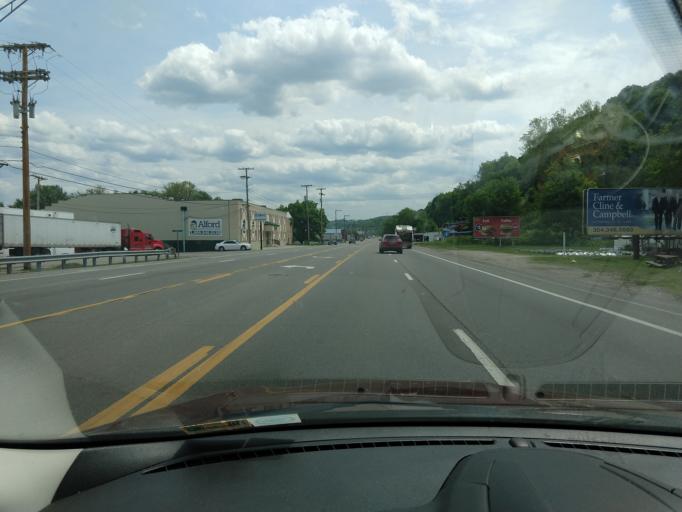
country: US
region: West Virginia
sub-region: Kanawha County
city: Dunbar
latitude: 38.3684
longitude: -81.7659
